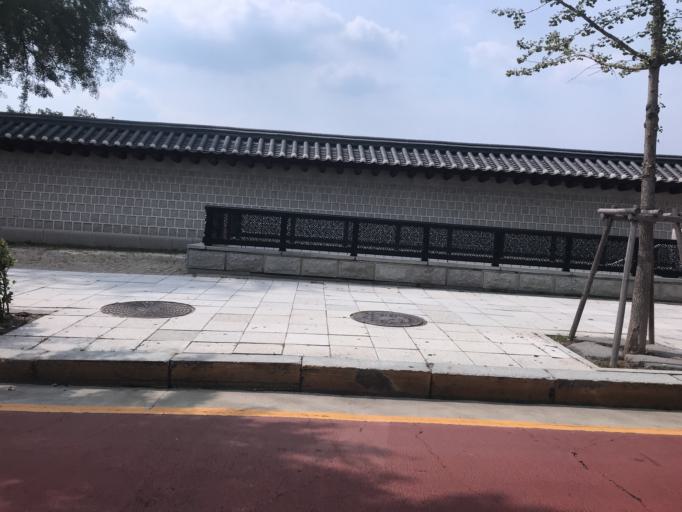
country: KR
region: Seoul
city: Seoul
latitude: 37.5762
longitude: 126.9793
